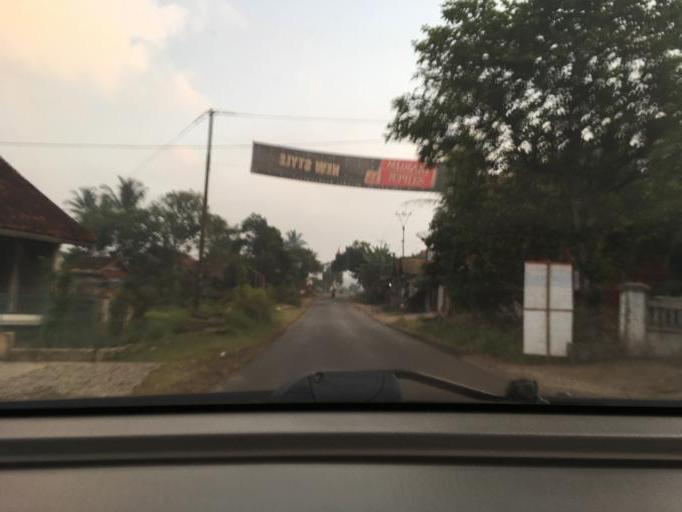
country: ID
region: West Java
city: Pasireurih
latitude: -7.1866
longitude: 108.1971
